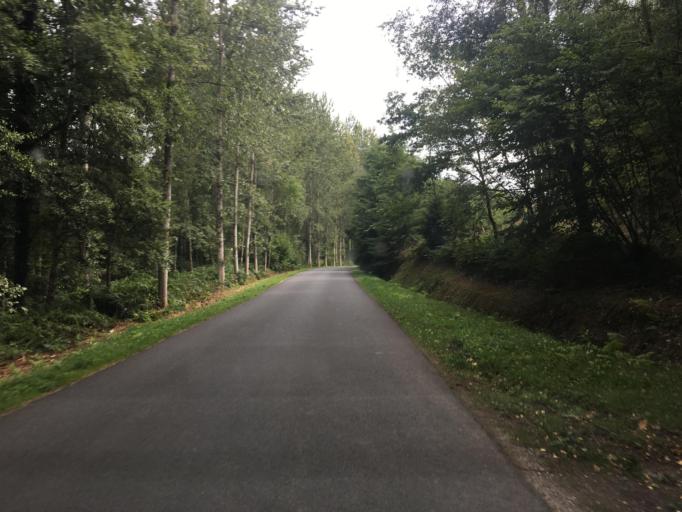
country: FR
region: Brittany
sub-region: Departement des Cotes-d'Armor
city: Gouarec
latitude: 48.2101
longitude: -3.1195
